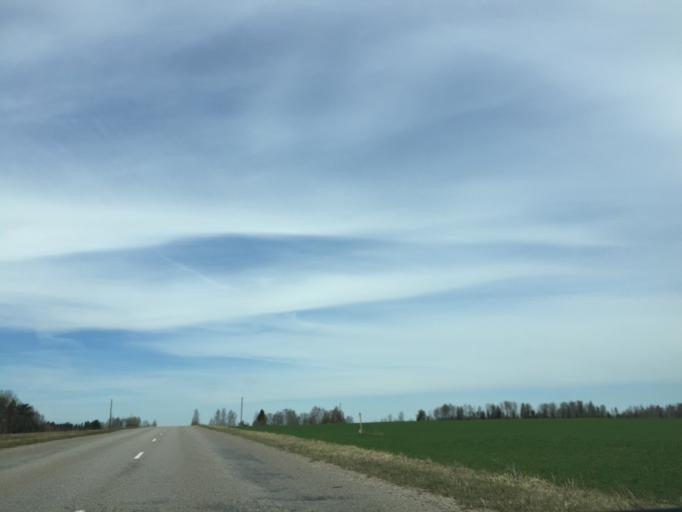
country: LV
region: Valkas Rajons
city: Valka
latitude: 57.7836
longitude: 25.9075
